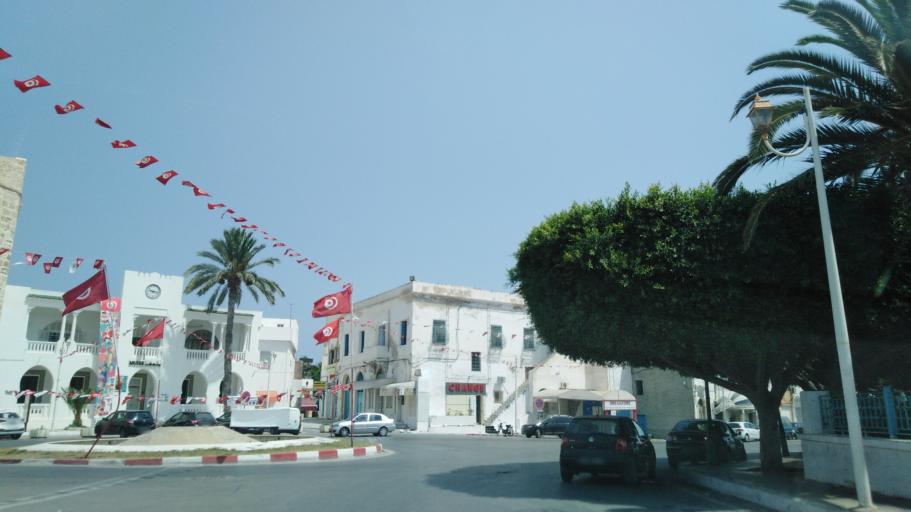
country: TN
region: Al Mahdiyah
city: Mahdia
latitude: 35.5038
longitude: 11.0680
